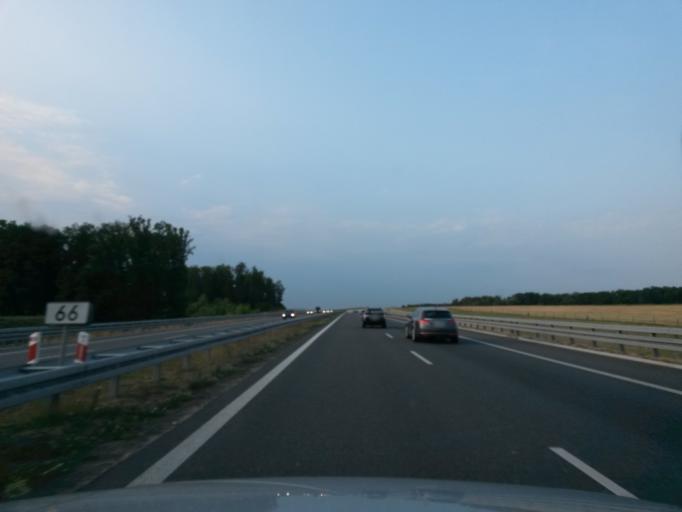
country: PL
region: Lower Silesian Voivodeship
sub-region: Powiat olesnicki
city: Twardogora
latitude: 51.2661
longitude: 17.5505
